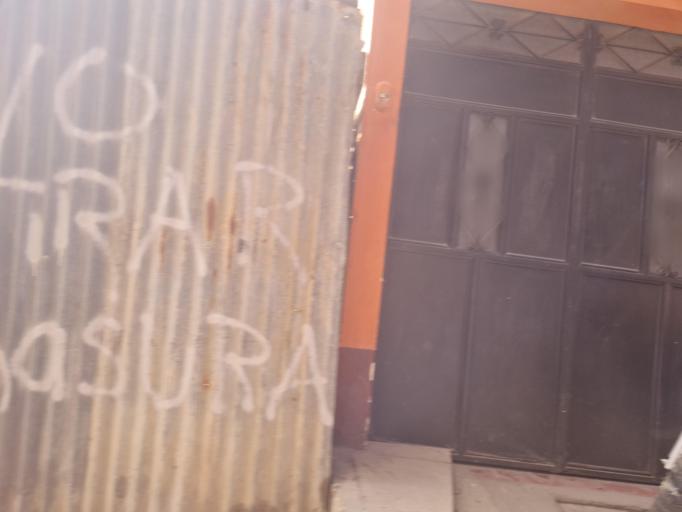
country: GT
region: Quetzaltenango
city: Quetzaltenango
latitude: 14.8383
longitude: -91.5355
